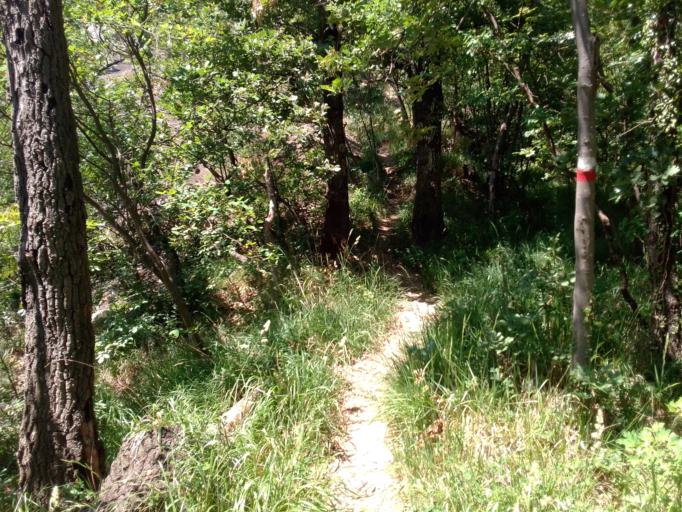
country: IT
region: Emilia-Romagna
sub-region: Provincia di Piacenza
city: Pianello Val Tidone
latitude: 44.9113
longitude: 9.3971
